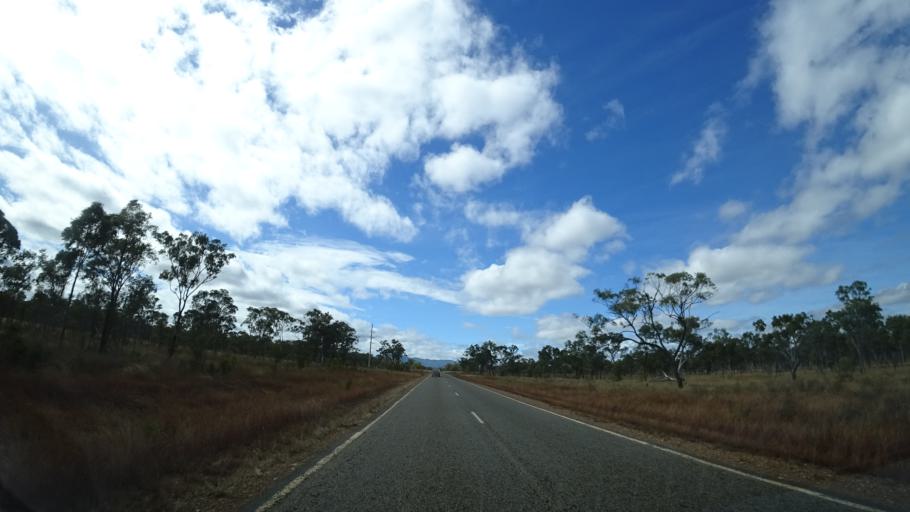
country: AU
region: Queensland
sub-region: Cairns
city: Port Douglas
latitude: -16.4971
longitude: 144.9864
